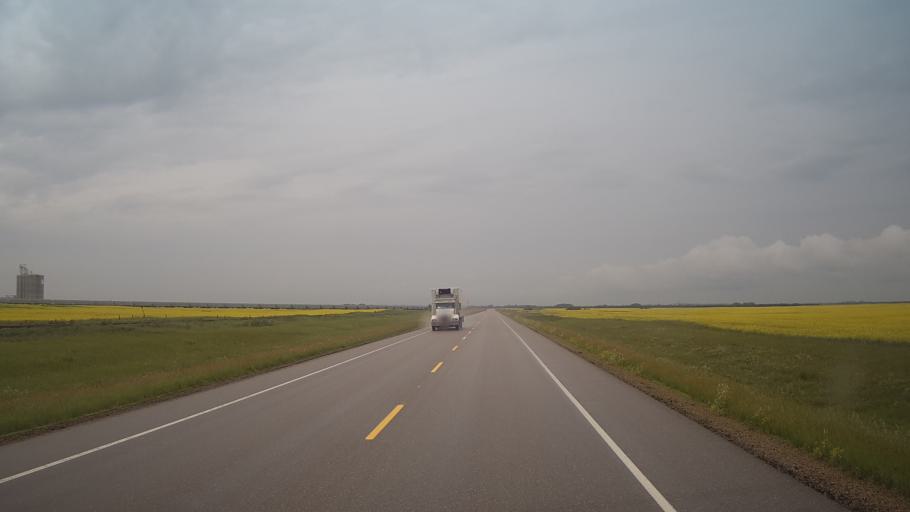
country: CA
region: Saskatchewan
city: Wilkie
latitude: 52.2997
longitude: -108.6721
